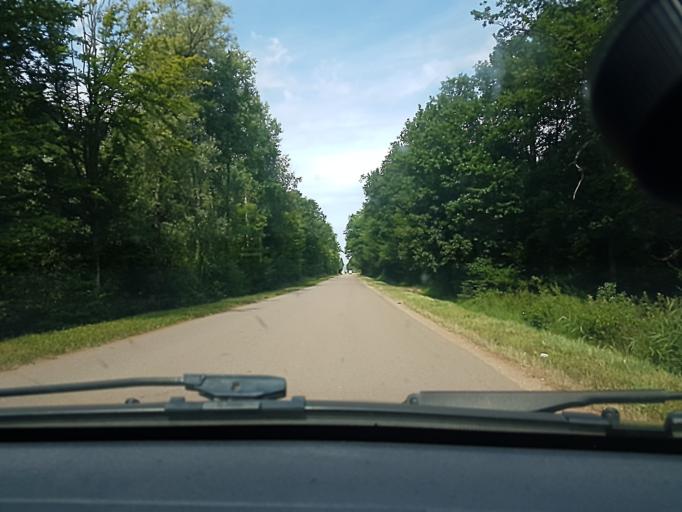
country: FR
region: Bourgogne
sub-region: Departement de Saone-et-Loire
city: Chagny
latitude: 46.8918
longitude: 4.7915
